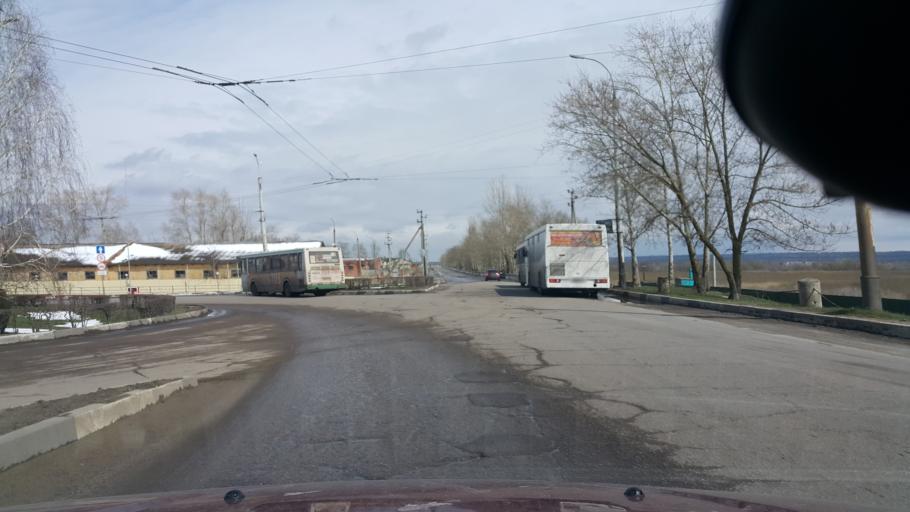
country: RU
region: Tambov
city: Bokino
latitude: 52.6736
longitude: 41.4662
